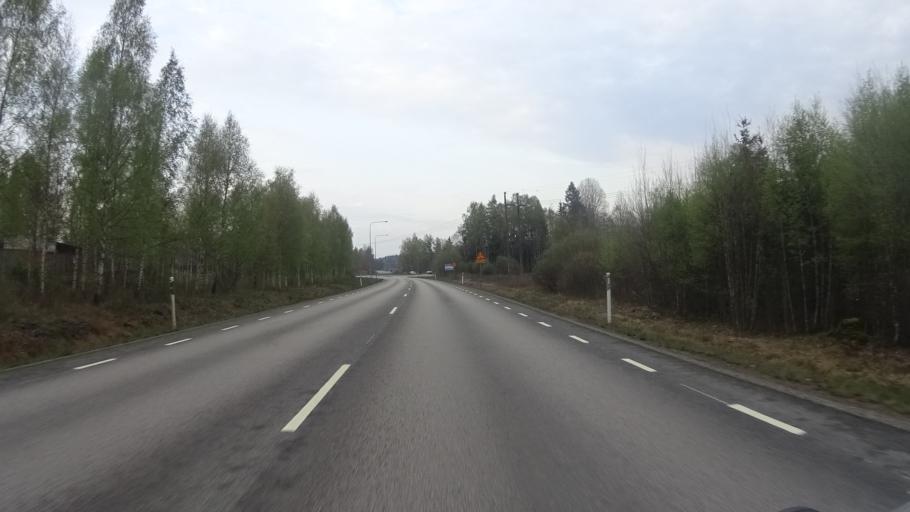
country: SE
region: Kronoberg
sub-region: Ljungby Kommun
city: Ljungby
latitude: 56.8262
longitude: 13.9666
